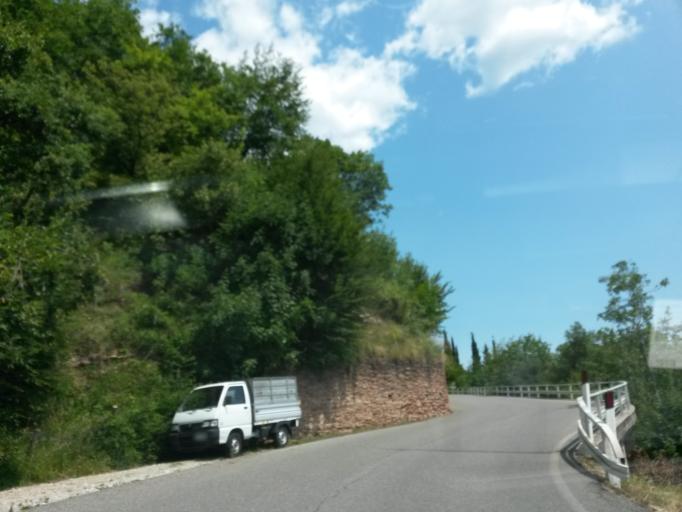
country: IT
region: Lombardy
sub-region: Provincia di Brescia
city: Gargnano
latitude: 45.6838
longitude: 10.6503
